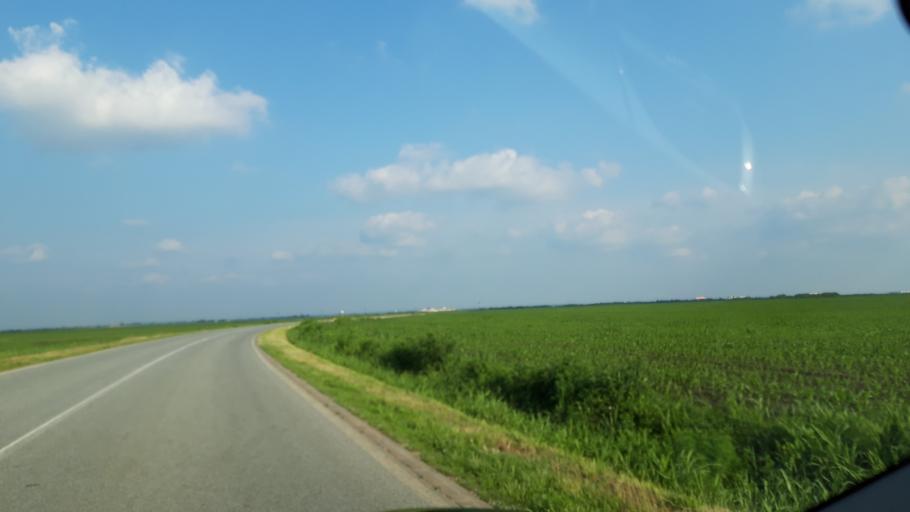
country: RS
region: Autonomna Pokrajina Vojvodina
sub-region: Sremski Okrug
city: Ingija
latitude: 45.0877
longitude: 20.1075
